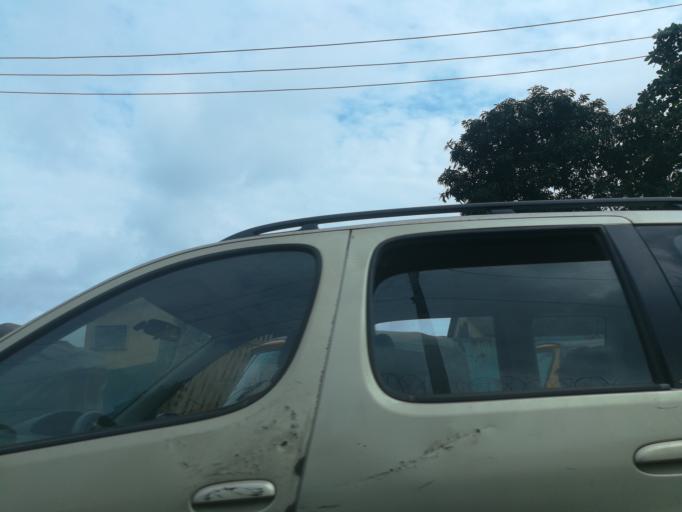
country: NG
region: Lagos
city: Agege
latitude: 6.6136
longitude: 3.3303
